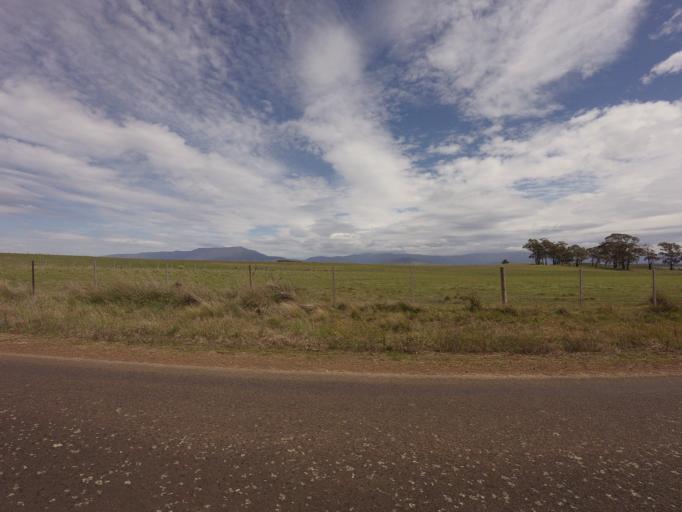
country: AU
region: Tasmania
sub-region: Northern Midlands
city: Longford
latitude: -41.7765
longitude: 147.2256
